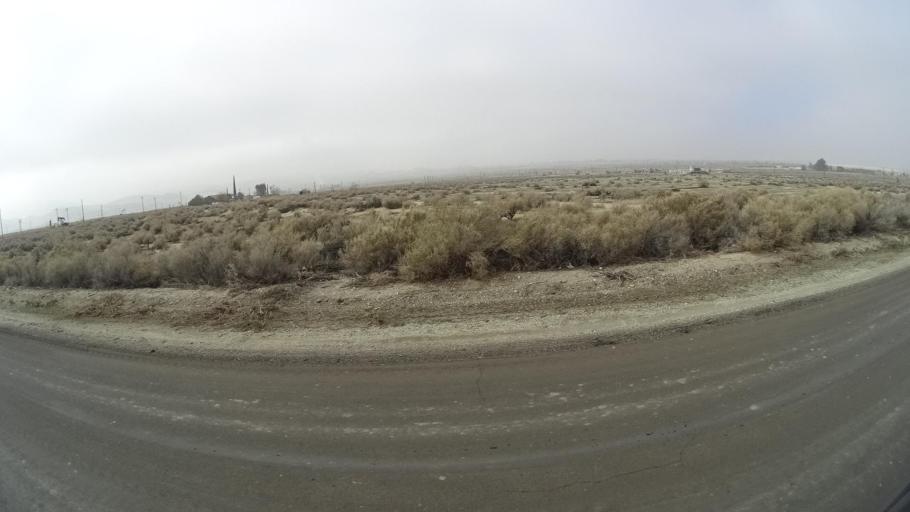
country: US
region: California
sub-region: Kern County
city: Maricopa
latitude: 35.0488
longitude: -119.3670
